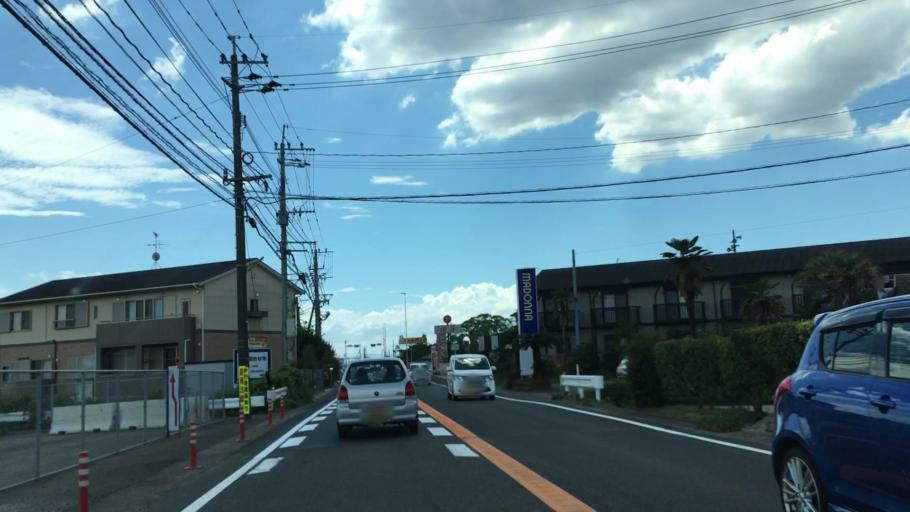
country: JP
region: Saga Prefecture
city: Kanzakimachi-kanzaki
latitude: 33.2879
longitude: 130.3510
